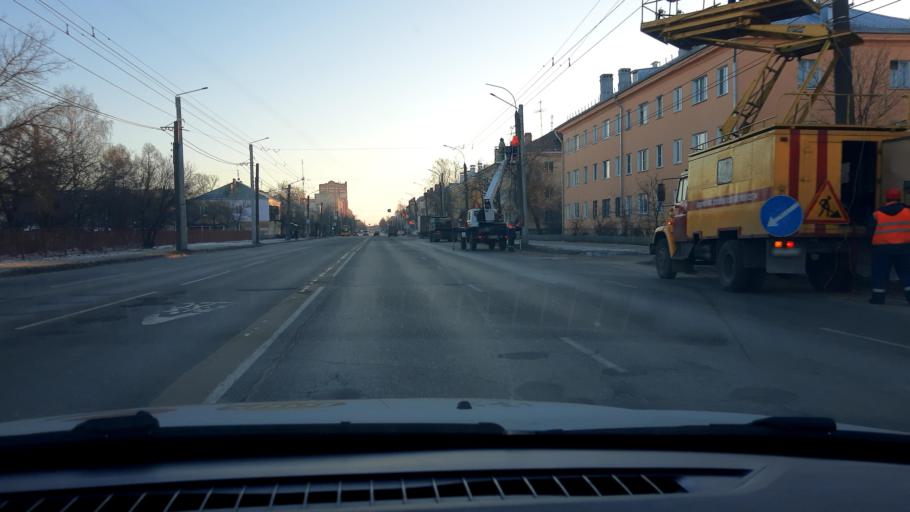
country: RU
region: Nizjnij Novgorod
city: Dzerzhinsk
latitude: 56.2495
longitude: 43.4536
